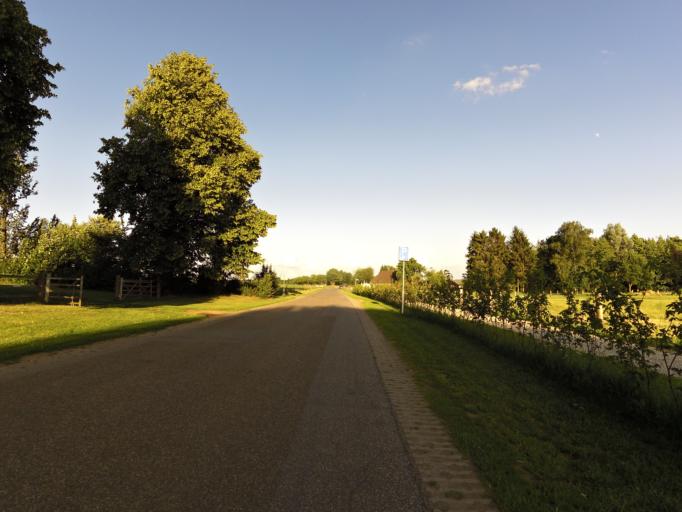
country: NL
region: Gelderland
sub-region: Oude IJsselstreek
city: Gendringen
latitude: 51.8716
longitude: 6.4175
